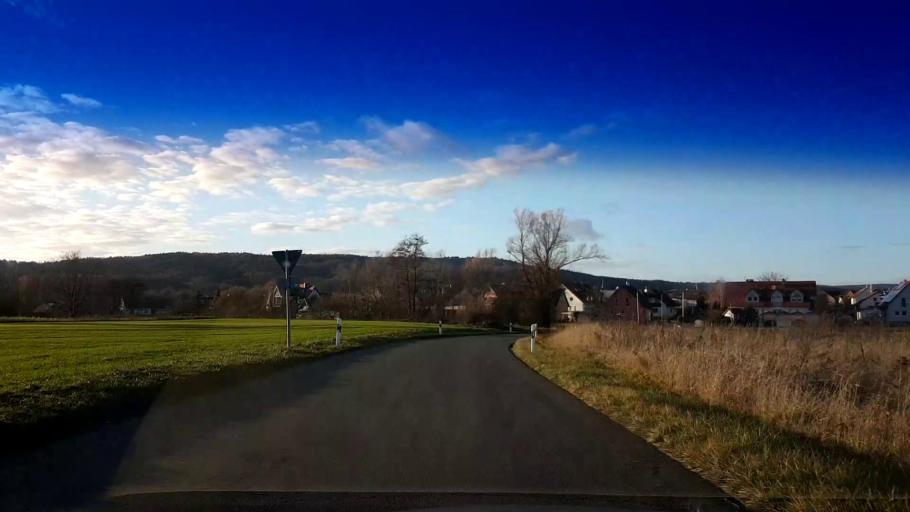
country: DE
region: Bavaria
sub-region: Upper Franconia
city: Hallstadt
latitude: 49.9305
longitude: 10.8804
